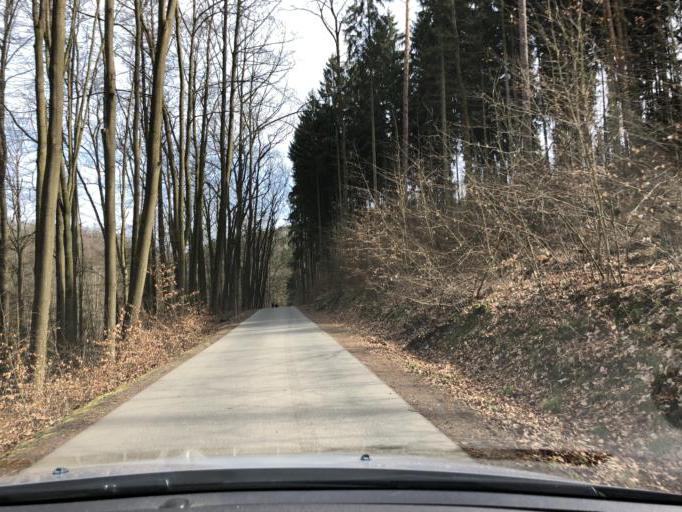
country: DE
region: Thuringia
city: Eisenberg
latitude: 50.9508
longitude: 11.9085
